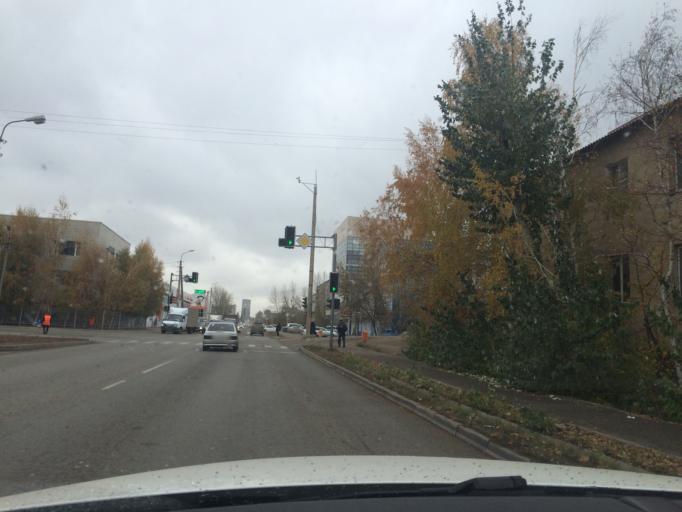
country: KZ
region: Astana Qalasy
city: Astana
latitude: 51.1720
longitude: 71.4522
